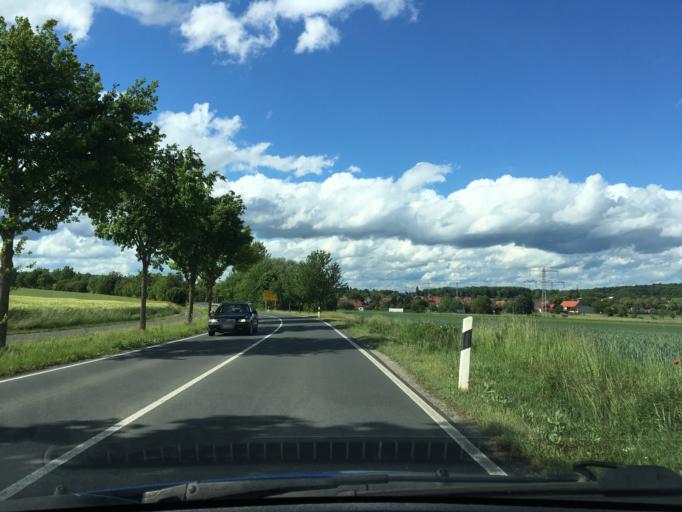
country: DE
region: Lower Saxony
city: Bovenden
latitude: 51.5762
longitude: 9.8763
